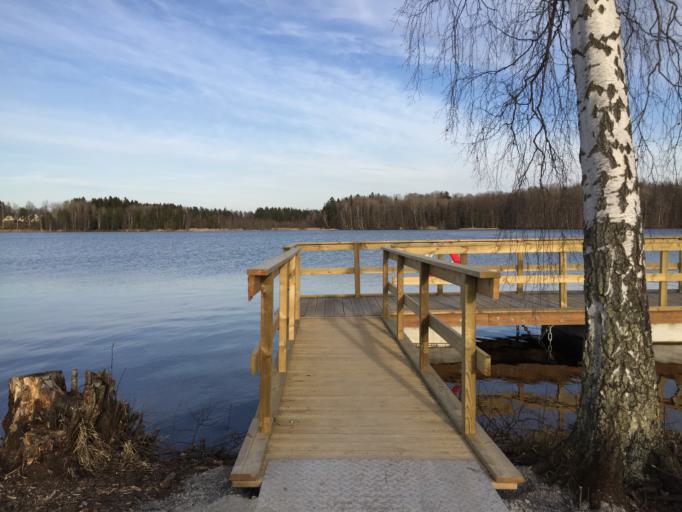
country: SE
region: Soedermanland
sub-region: Katrineholms Kommun
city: Katrineholm
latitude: 58.9741
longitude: 16.1887
